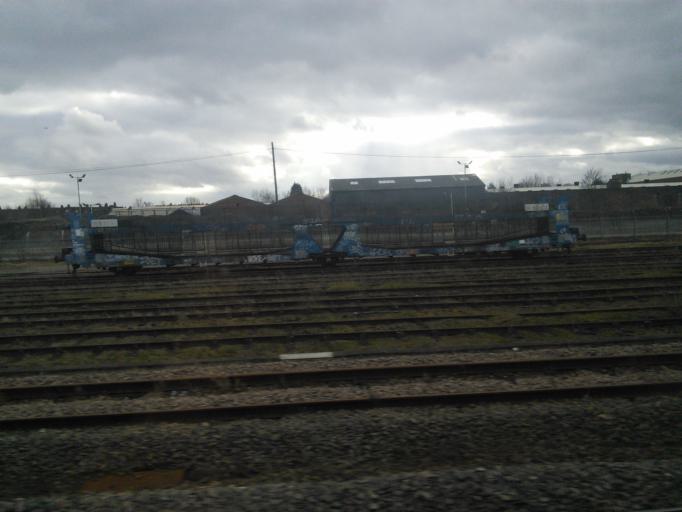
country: GB
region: England
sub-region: City and Borough of Birmingham
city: Birmingham
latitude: 52.4651
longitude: -1.8634
